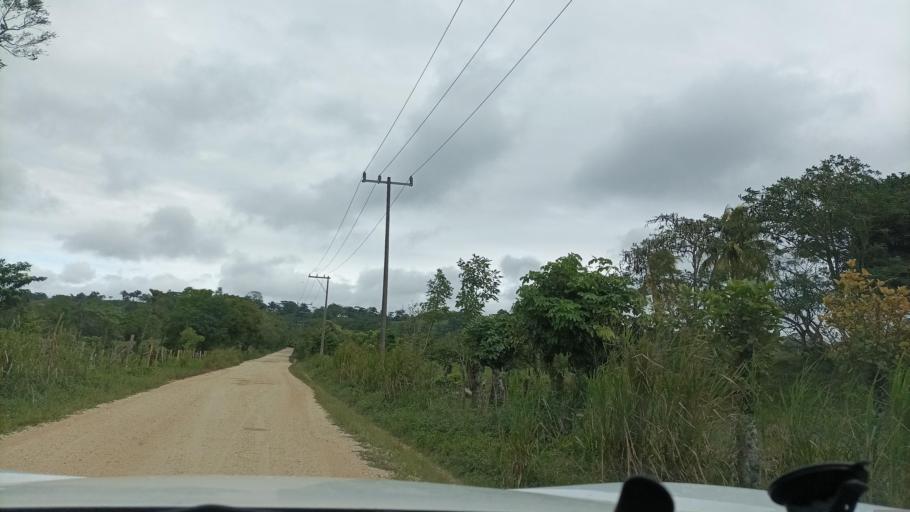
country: MX
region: Veracruz
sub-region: Moloacan
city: Cuichapa
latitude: 17.8290
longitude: -94.3542
